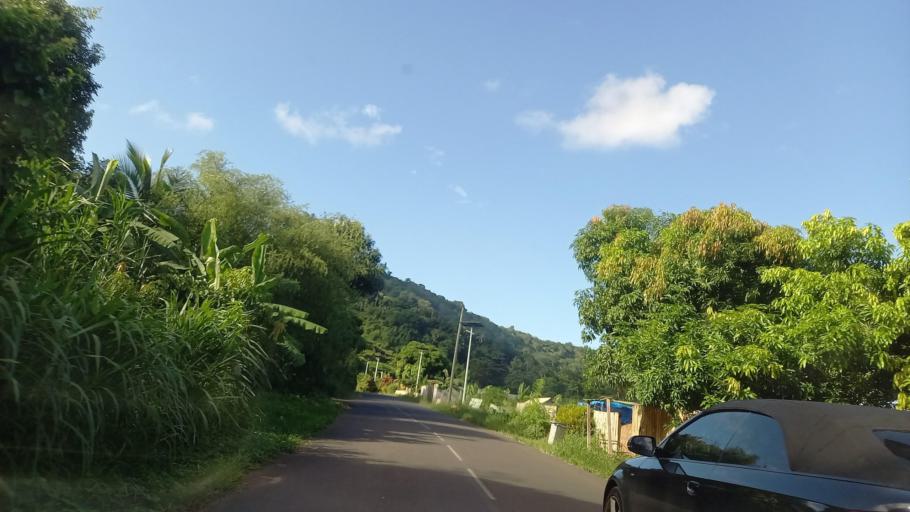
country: YT
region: Kani-Keli
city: Kani Keli
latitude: -12.9640
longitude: 45.1134
